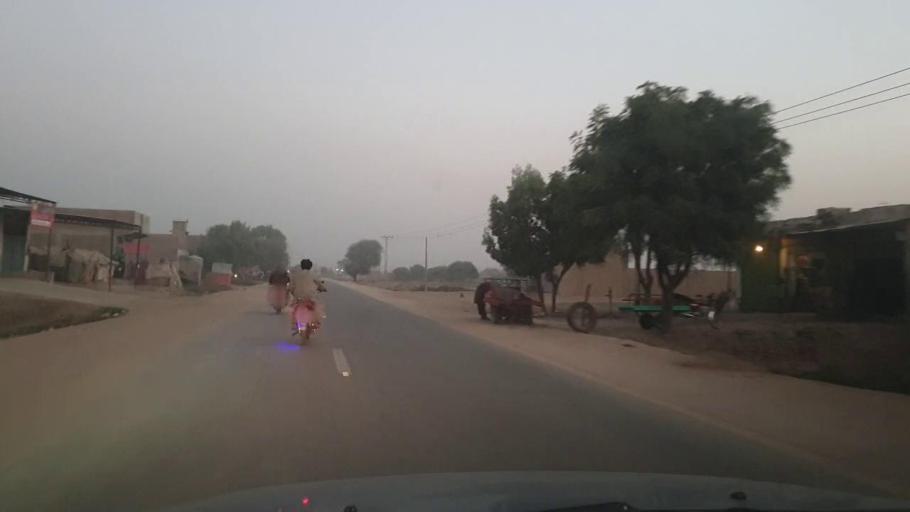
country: PK
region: Sindh
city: Tando Allahyar
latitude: 25.4480
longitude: 68.7290
